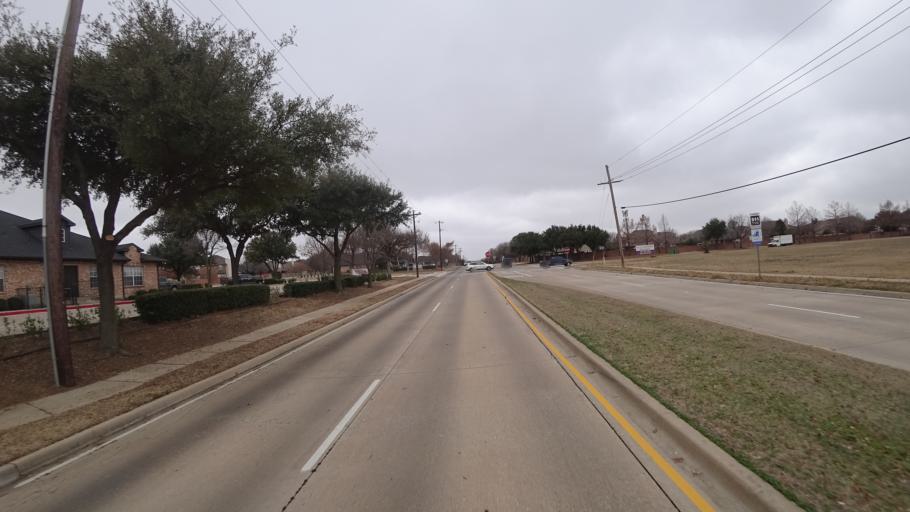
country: US
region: Texas
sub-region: Denton County
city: Lewisville
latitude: 33.0207
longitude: -97.0360
